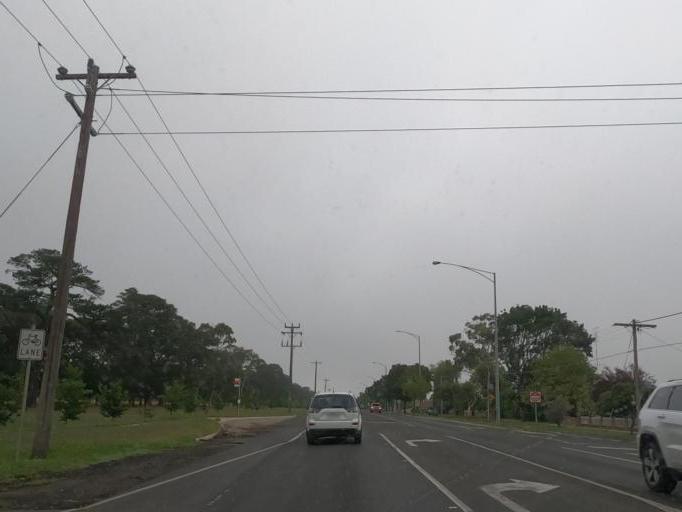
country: AU
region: Victoria
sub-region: Ballarat North
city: Newington
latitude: -37.5569
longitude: 143.8186
